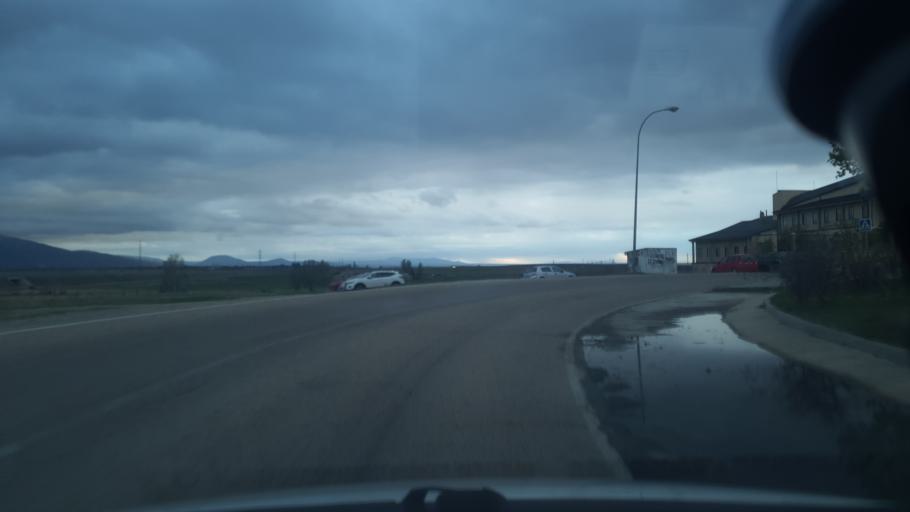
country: ES
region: Castille and Leon
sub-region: Provincia de Segovia
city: San Cristobal de Segovia
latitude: 40.9267
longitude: -4.0923
